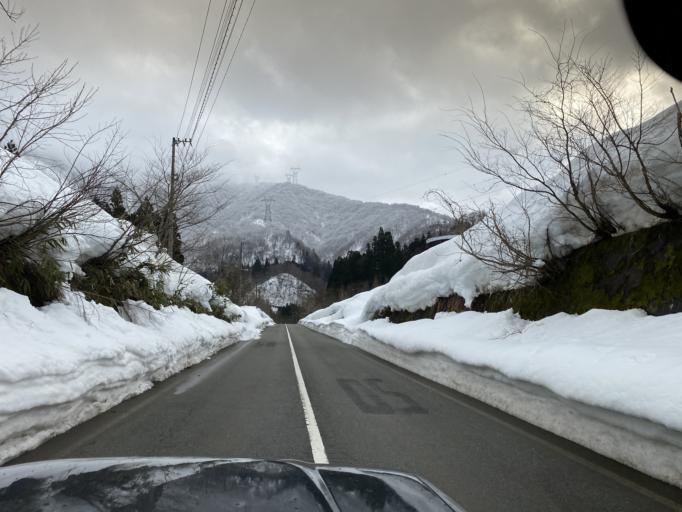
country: JP
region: Toyama
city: Fukumitsu
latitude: 36.3206
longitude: 136.8984
